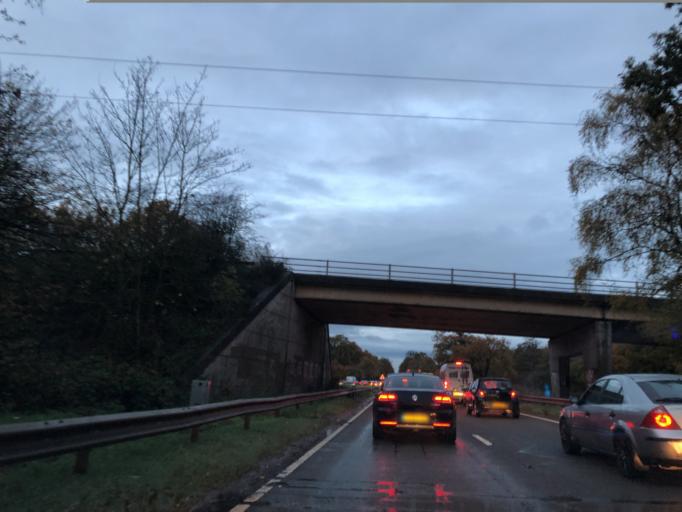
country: GB
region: England
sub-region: Solihull
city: Bickenhill
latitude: 52.4663
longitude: -1.7046
